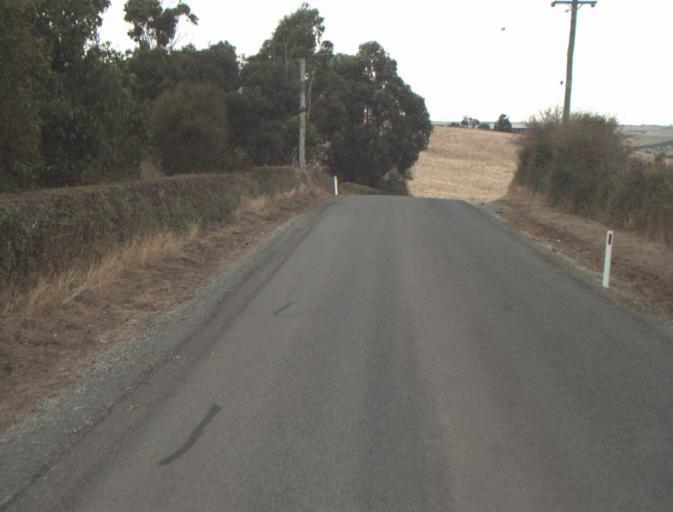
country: AU
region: Tasmania
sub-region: Northern Midlands
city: Evandale
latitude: -41.5215
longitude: 147.2471
